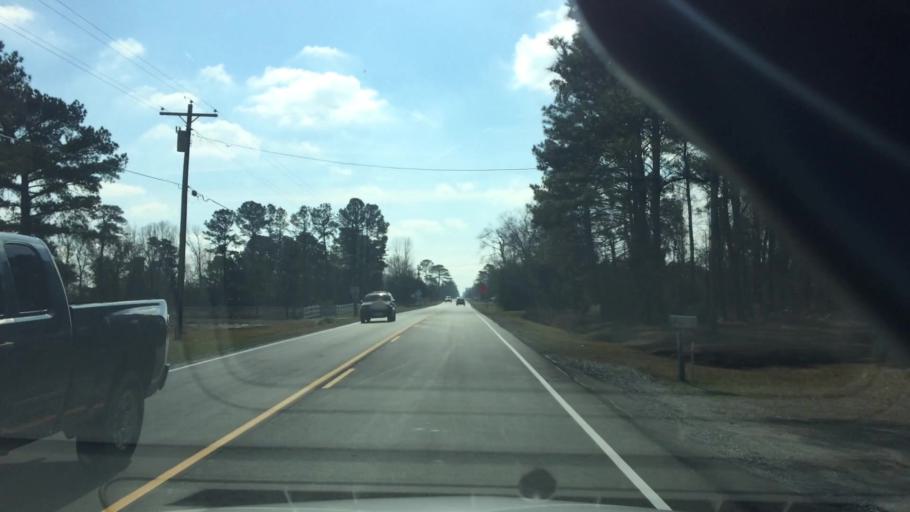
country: US
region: North Carolina
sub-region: Duplin County
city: Beulaville
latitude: 35.0020
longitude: -77.7548
